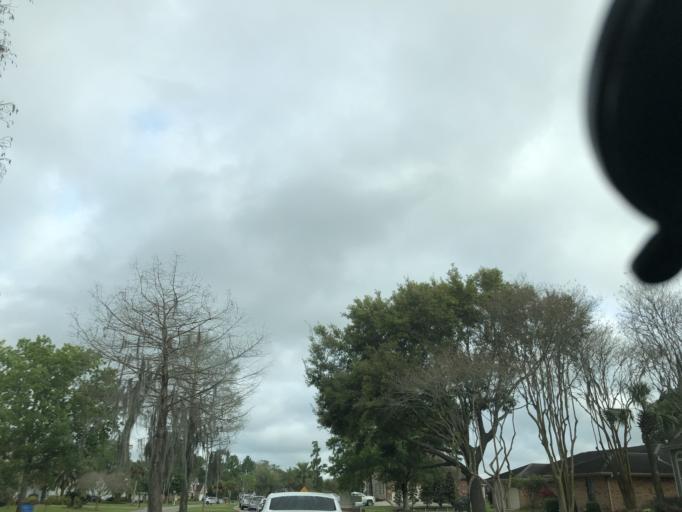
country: US
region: Louisiana
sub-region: Saint Charles Parish
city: New Sarpy
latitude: 29.9821
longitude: -90.3631
